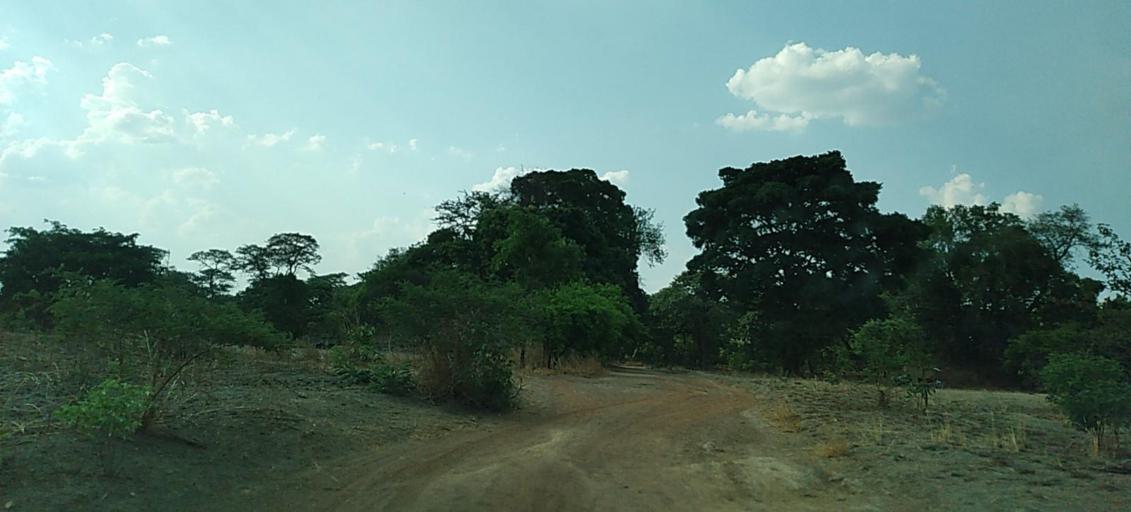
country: ZM
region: Copperbelt
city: Mpongwe
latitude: -13.4787
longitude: 28.0833
